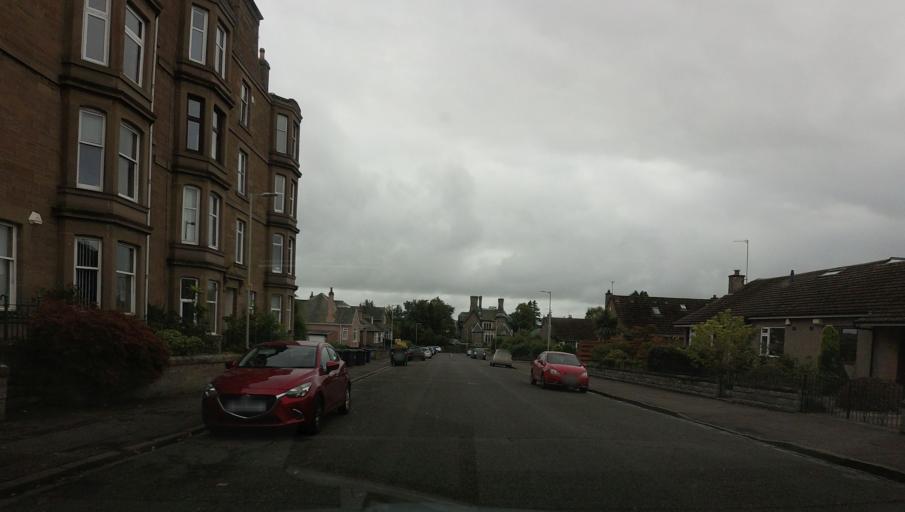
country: GB
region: Scotland
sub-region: Dundee City
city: Dundee
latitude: 56.4582
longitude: -2.9996
